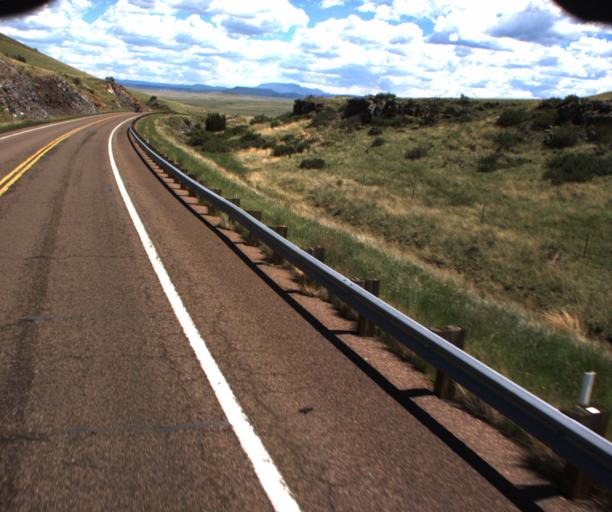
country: US
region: Arizona
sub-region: Apache County
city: Springerville
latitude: 34.2117
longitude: -109.4290
